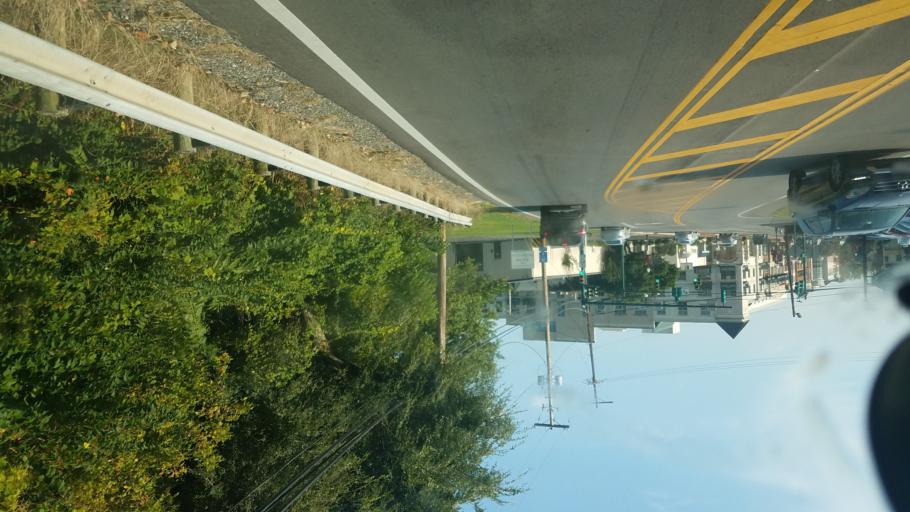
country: US
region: Ohio
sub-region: Franklin County
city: Gahanna
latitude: 40.0230
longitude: -82.8792
